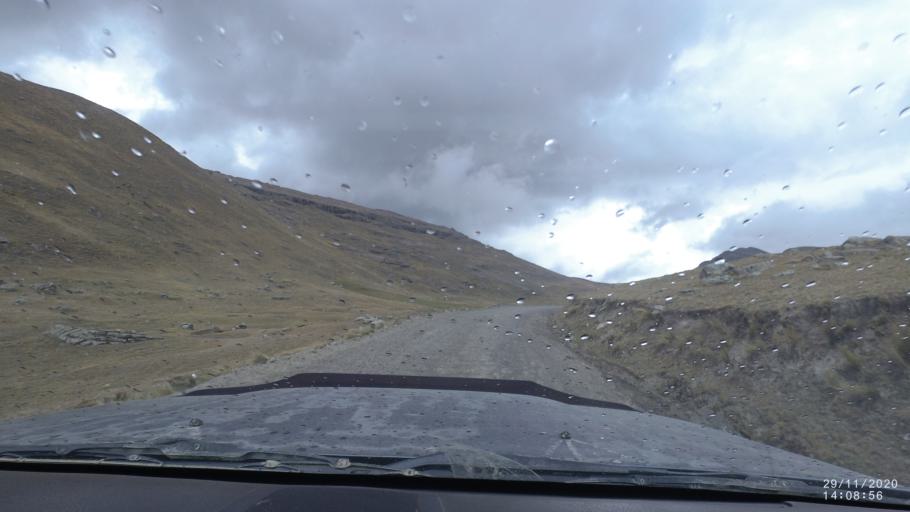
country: BO
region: Cochabamba
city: Sipe Sipe
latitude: -17.2246
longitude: -66.3826
